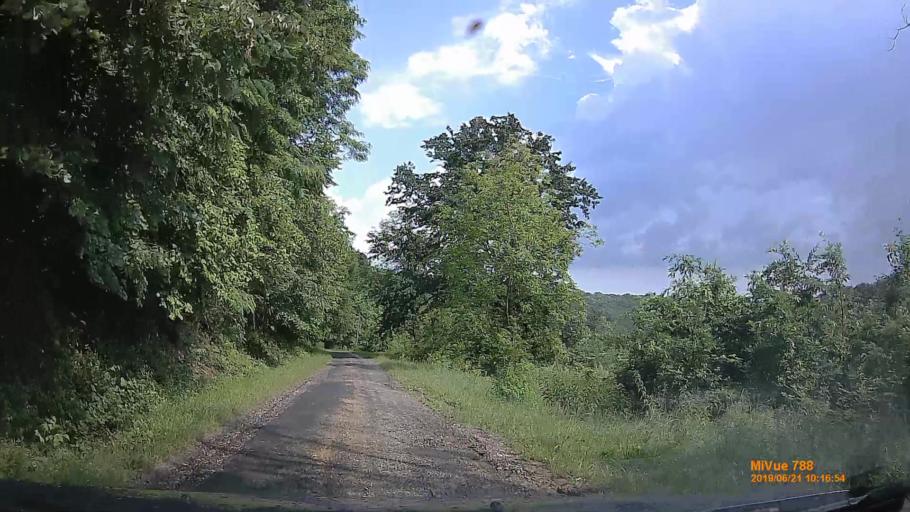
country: HU
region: Baranya
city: Buekkoesd
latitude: 46.1937
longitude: 17.9588
